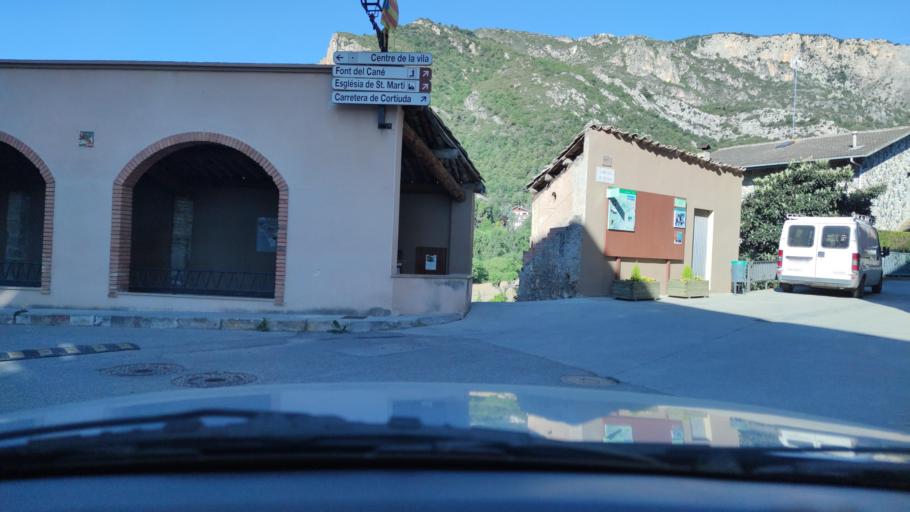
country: ES
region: Catalonia
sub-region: Provincia de Lleida
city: Oliana
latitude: 42.0586
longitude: 1.2674
